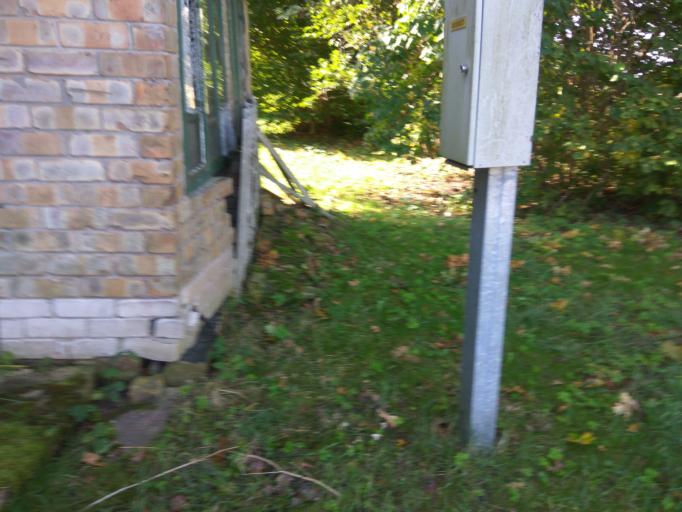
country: LV
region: Ventspils
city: Ventspils
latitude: 57.3562
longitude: 21.6637
